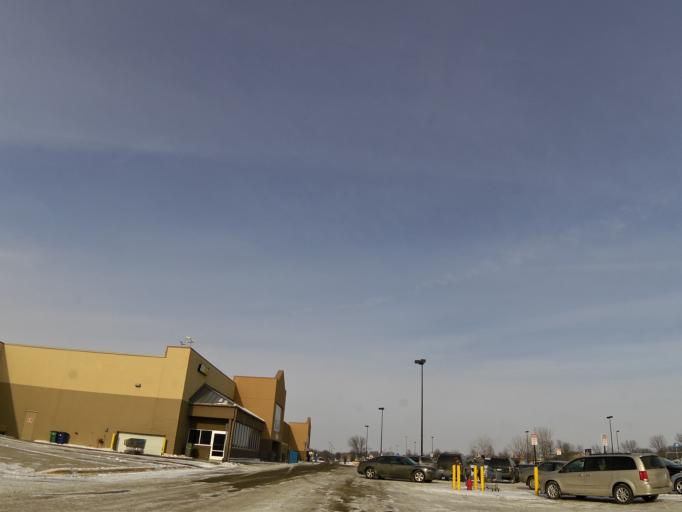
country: US
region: Minnesota
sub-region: McLeod County
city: Hutchinson
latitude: 44.8709
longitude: -94.3780
